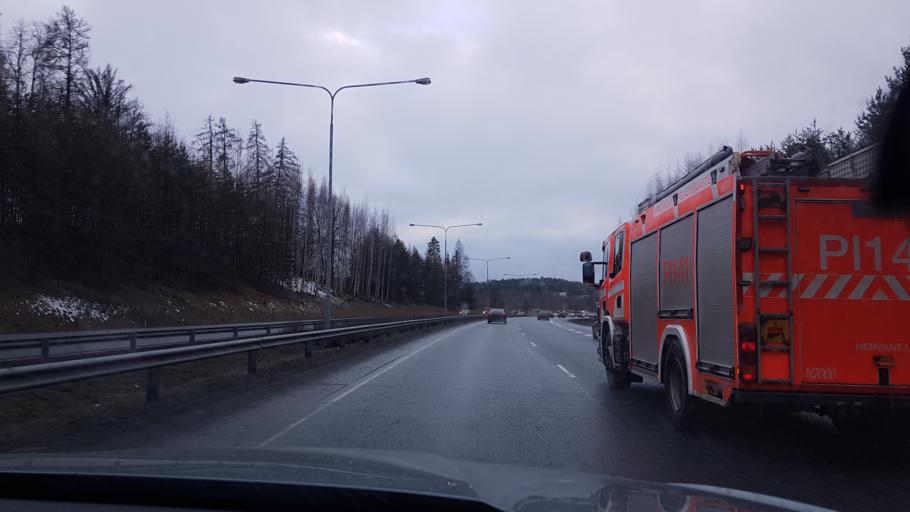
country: FI
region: Pirkanmaa
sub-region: Tampere
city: Tampere
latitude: 61.4732
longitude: 23.8660
